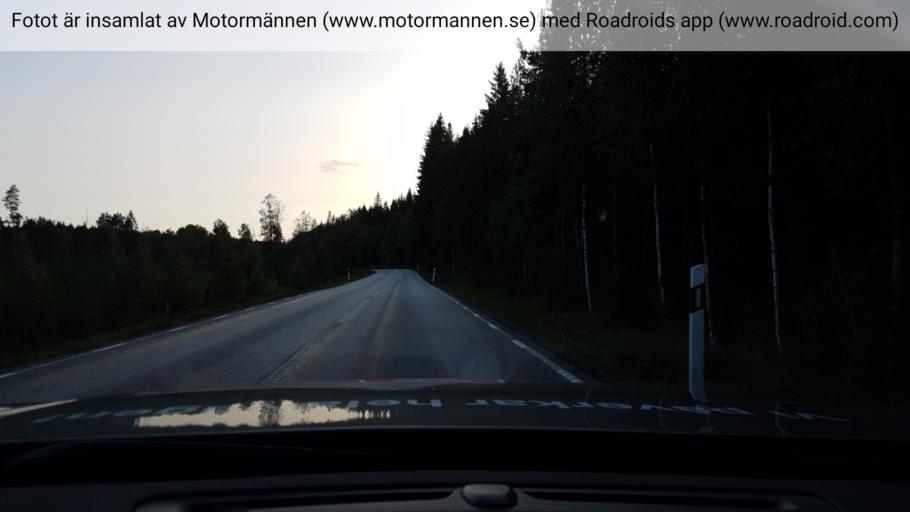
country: SE
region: OErebro
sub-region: Ljusnarsbergs Kommun
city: Kopparberg
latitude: 59.8213
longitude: 14.9671
